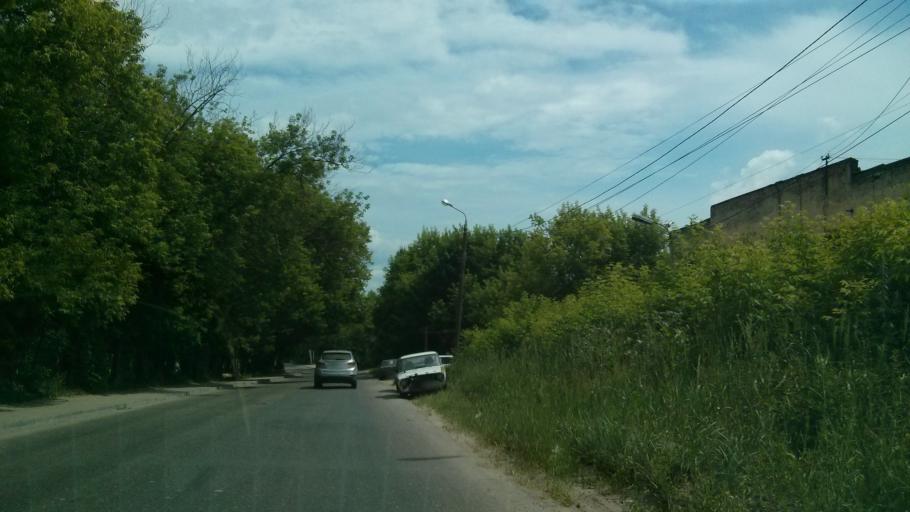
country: RU
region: Nizjnij Novgorod
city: Nizhniy Novgorod
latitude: 56.2985
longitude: 44.0002
